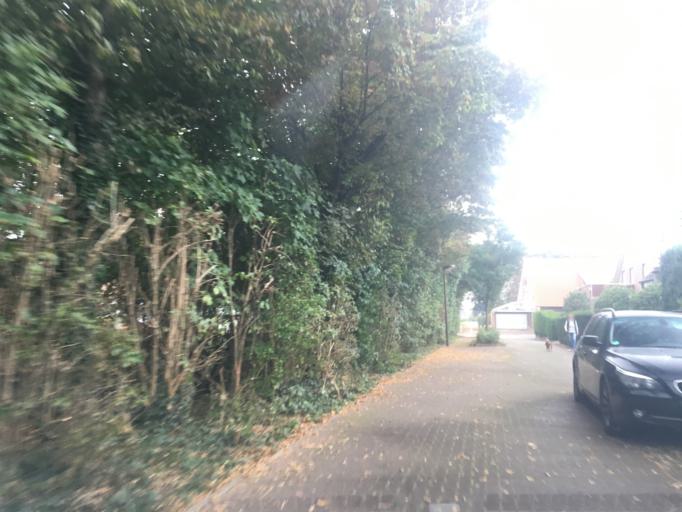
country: DE
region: North Rhine-Westphalia
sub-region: Regierungsbezirk Munster
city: Altenberge
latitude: 52.0396
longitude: 7.4697
